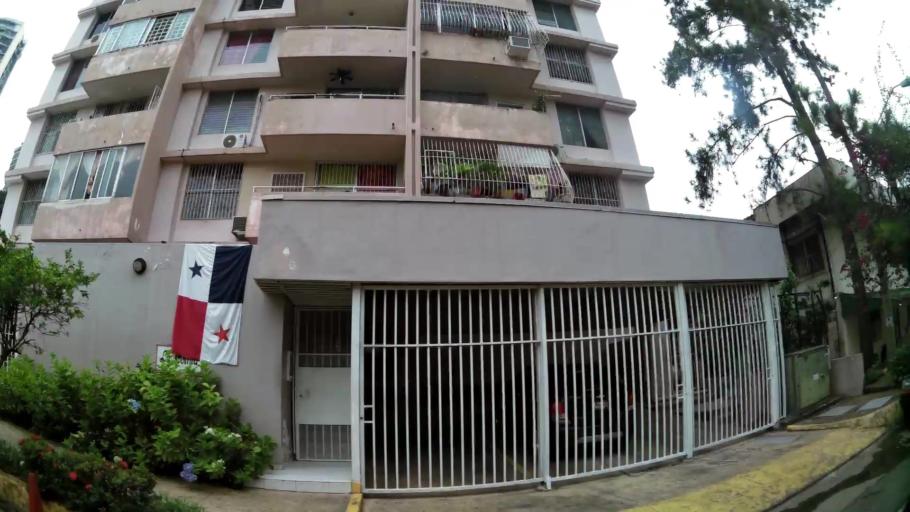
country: PA
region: Panama
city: Panama
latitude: 8.9828
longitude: -79.5312
